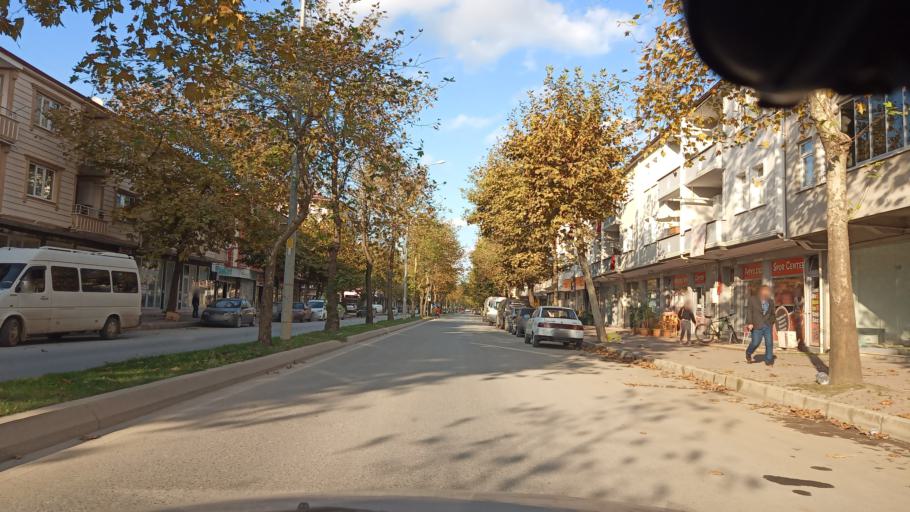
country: TR
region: Sakarya
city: Karasu
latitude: 41.0982
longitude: 30.6882
